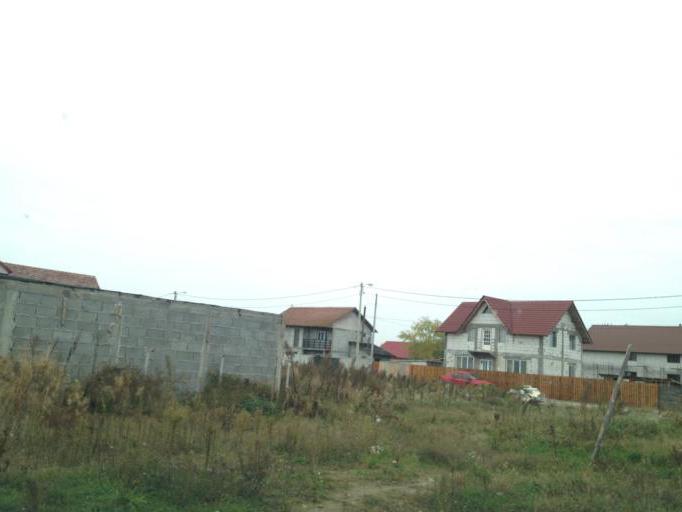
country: RO
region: Dolj
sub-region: Municipiul Craiova
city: Popoveni
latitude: 44.2923
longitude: 23.7830
